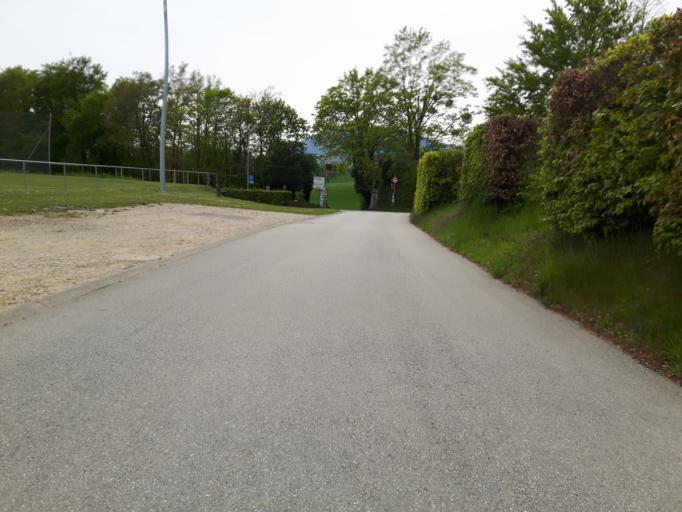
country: CH
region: Neuchatel
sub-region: Boudry District
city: Gorgier
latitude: 46.9118
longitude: 6.7884
